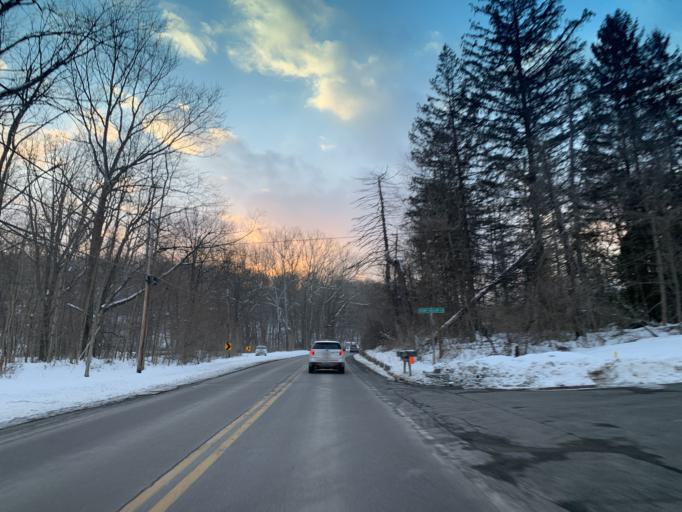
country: US
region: Maryland
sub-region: Allegany County
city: La Vale
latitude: 39.6982
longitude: -78.8617
